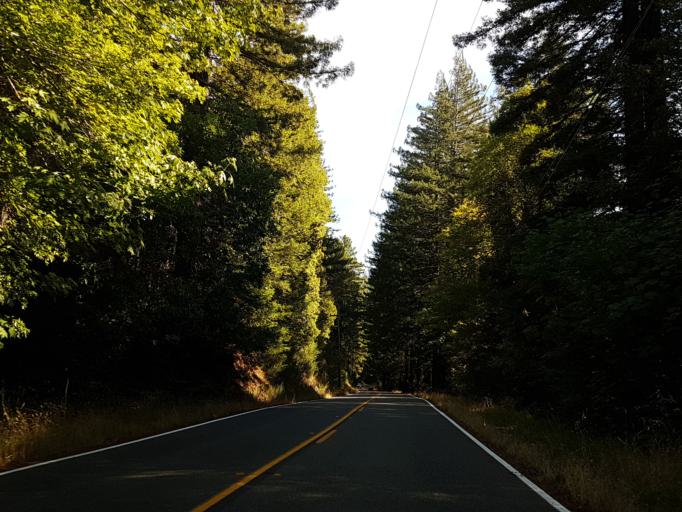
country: US
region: California
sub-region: Humboldt County
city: Rio Dell
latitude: 40.4116
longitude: -123.9583
